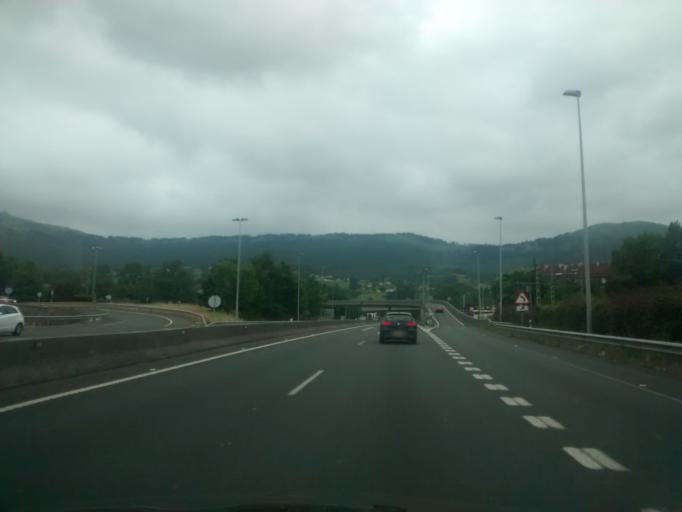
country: ES
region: Cantabria
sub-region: Provincia de Cantabria
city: El Astillero
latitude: 43.3997
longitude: -3.8157
